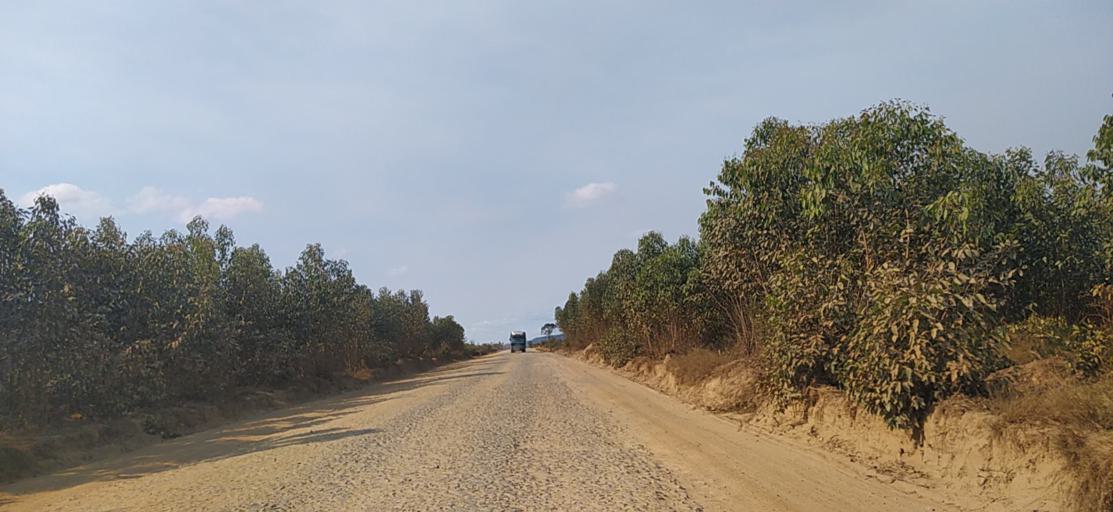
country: MG
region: Alaotra Mangoro
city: Moramanga
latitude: -18.6815
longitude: 48.2721
